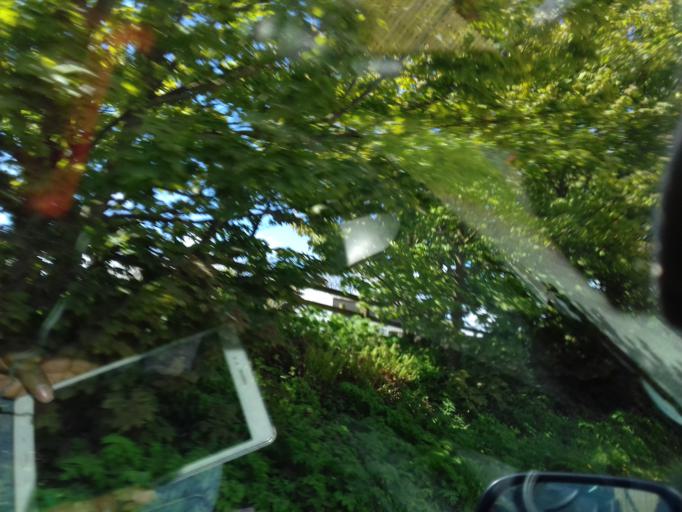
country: IE
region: Leinster
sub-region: Loch Garman
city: Castlebridge
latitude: 52.3896
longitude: -6.3727
